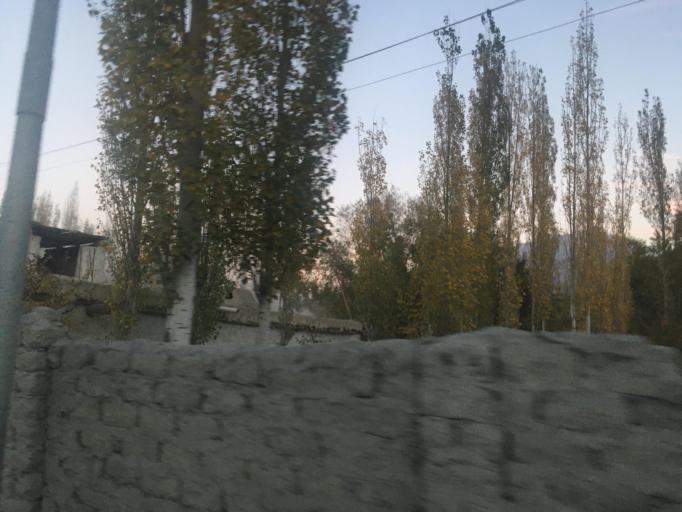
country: PK
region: Gilgit-Baltistan
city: Skardu
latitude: 35.2991
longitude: 75.5480
